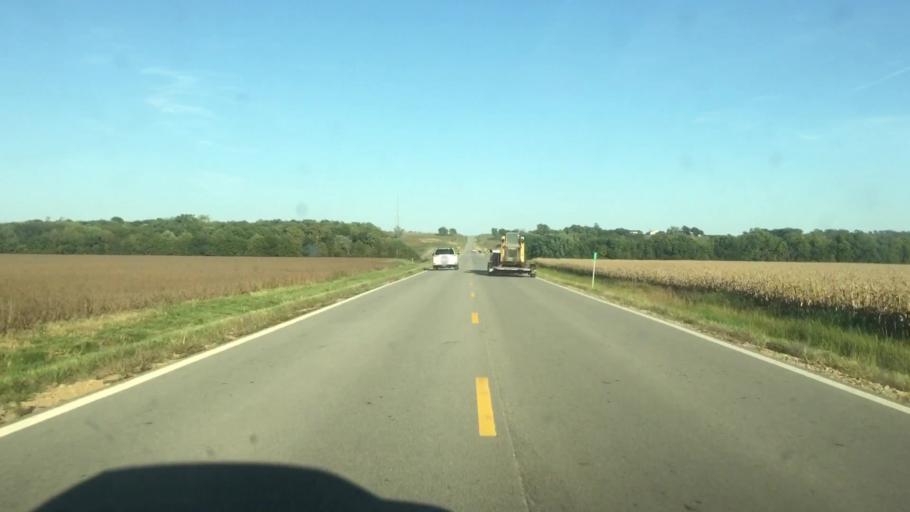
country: US
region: Kansas
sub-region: Brown County
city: Horton
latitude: 39.5875
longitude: -95.5615
